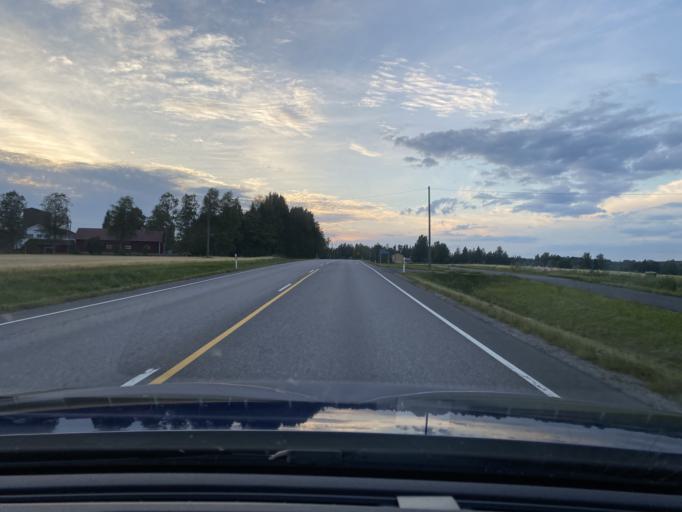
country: FI
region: Satakunta
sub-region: Pohjois-Satakunta
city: Kankaanpaeae
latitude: 61.7523
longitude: 22.5117
